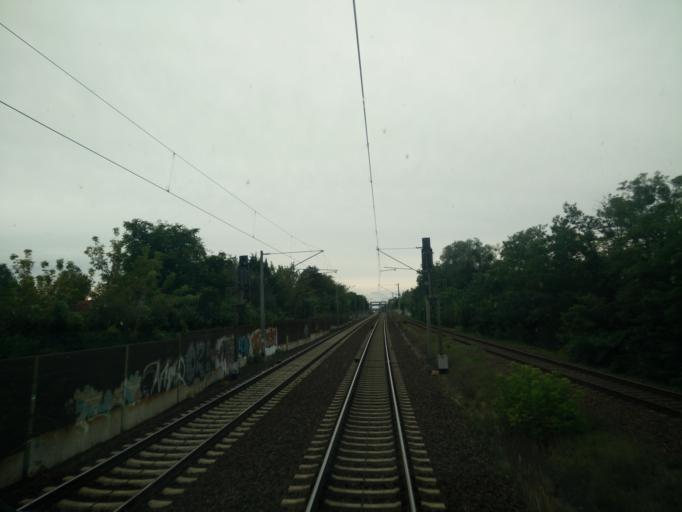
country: DE
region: Brandenburg
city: Brieselang
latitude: 52.5869
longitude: 12.9844
